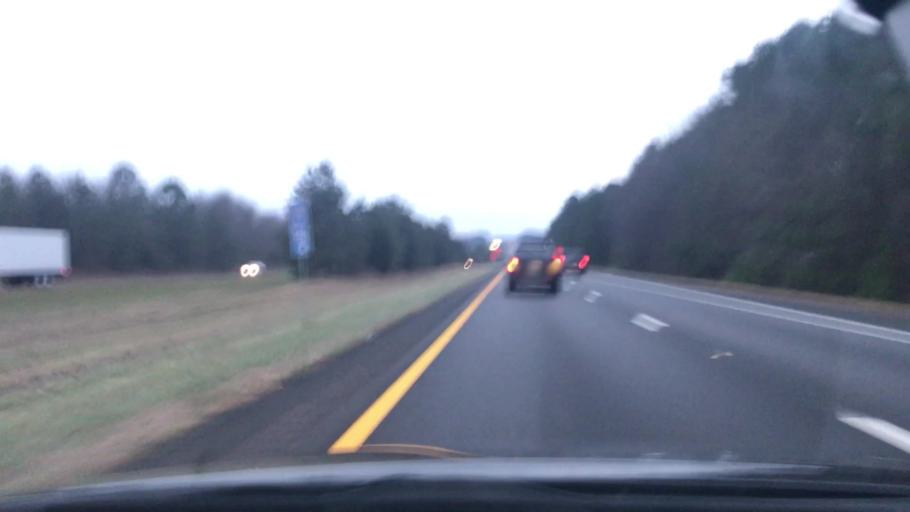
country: US
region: Tennessee
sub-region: Sumner County
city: White House
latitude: 36.4498
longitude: -86.6968
